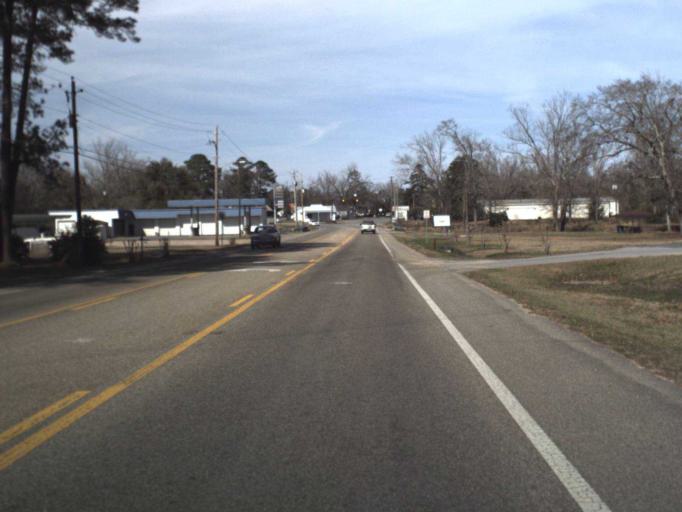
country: US
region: Florida
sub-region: Jackson County
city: Graceville
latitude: 30.9483
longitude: -85.5157
